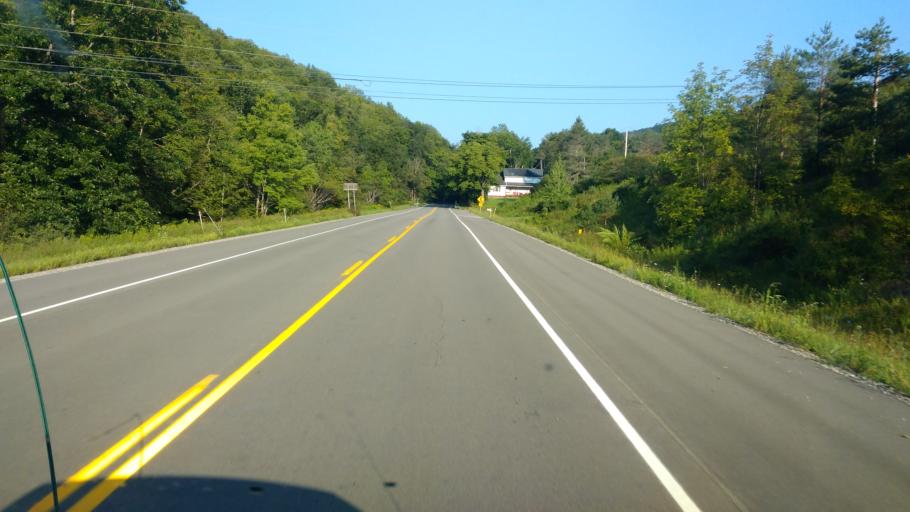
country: US
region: New York
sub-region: Allegany County
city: Andover
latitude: 42.1385
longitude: -77.6602
